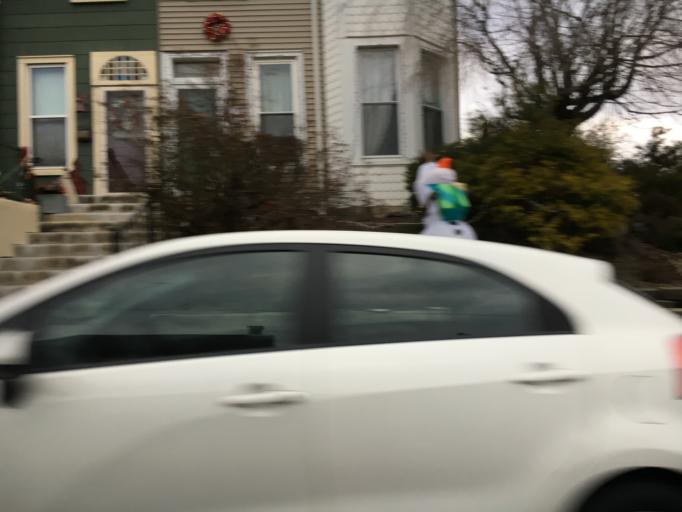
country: US
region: Pennsylvania
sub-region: Northampton County
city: Northampton
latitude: 40.6921
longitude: -75.4999
